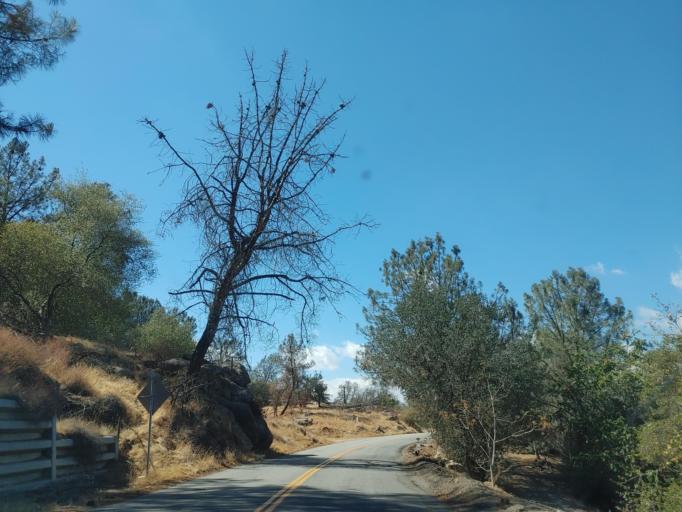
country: US
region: California
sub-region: Kern County
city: Bear Valley Springs
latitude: 35.2227
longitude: -118.5601
